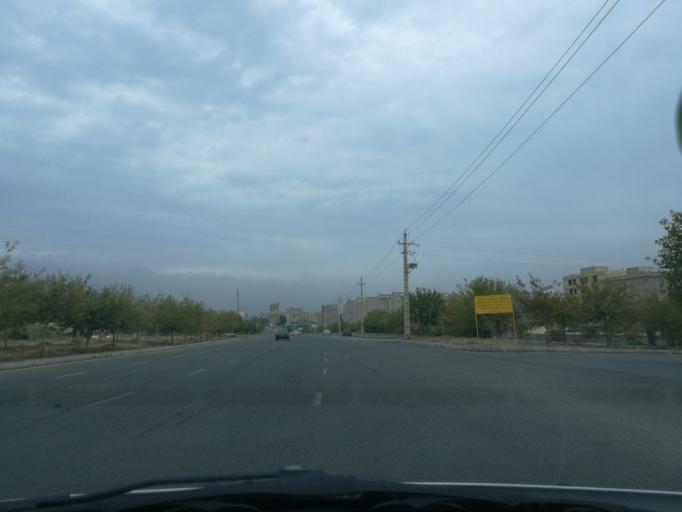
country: IR
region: Alborz
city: Karaj
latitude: 35.8639
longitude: 50.9298
